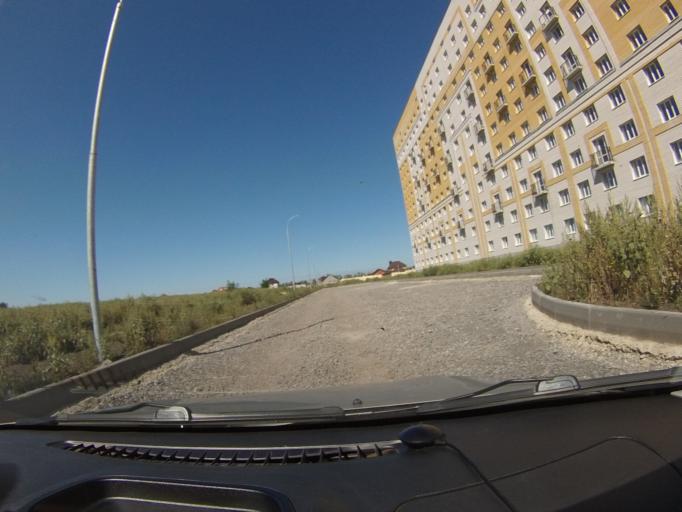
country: RU
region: Tambov
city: Tambov
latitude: 52.7787
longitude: 41.4064
